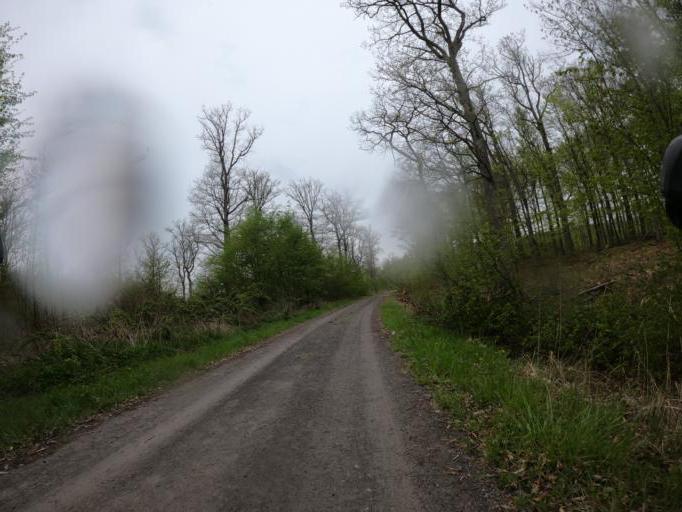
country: DE
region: Baden-Wuerttemberg
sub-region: Karlsruhe Region
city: Illingen
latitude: 48.9751
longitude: 8.8888
